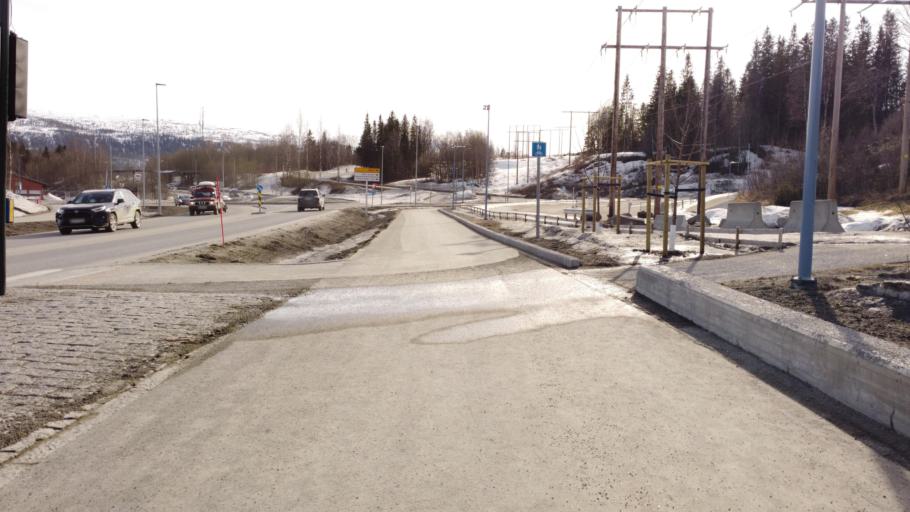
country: NO
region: Nordland
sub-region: Rana
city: Mo i Rana
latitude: 66.3289
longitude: 14.1597
